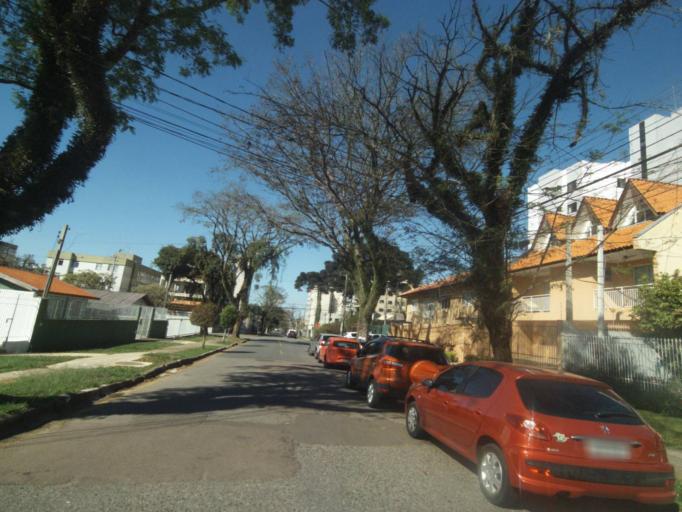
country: BR
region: Parana
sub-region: Curitiba
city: Curitiba
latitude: -25.3993
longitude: -49.2408
